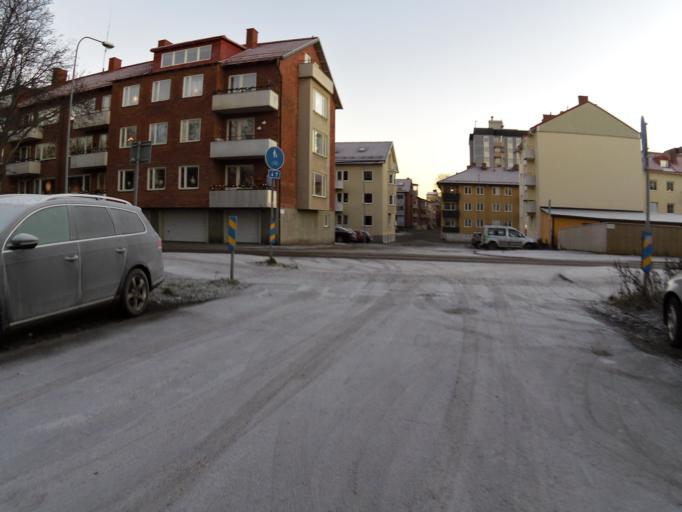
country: SE
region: Gaevleborg
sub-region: Gavle Kommun
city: Gavle
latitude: 60.6683
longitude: 17.1439
